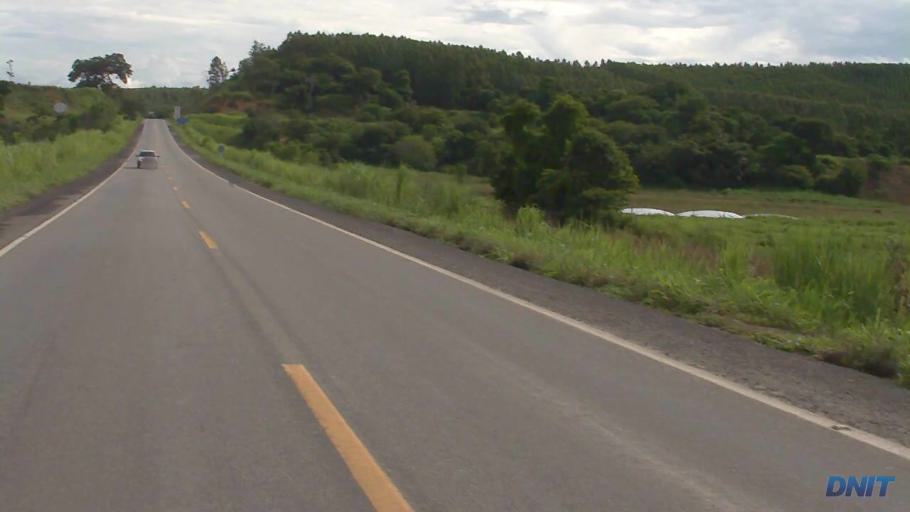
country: BR
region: Minas Gerais
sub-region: Belo Oriente
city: Belo Oriente
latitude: -19.2426
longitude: -42.3356
